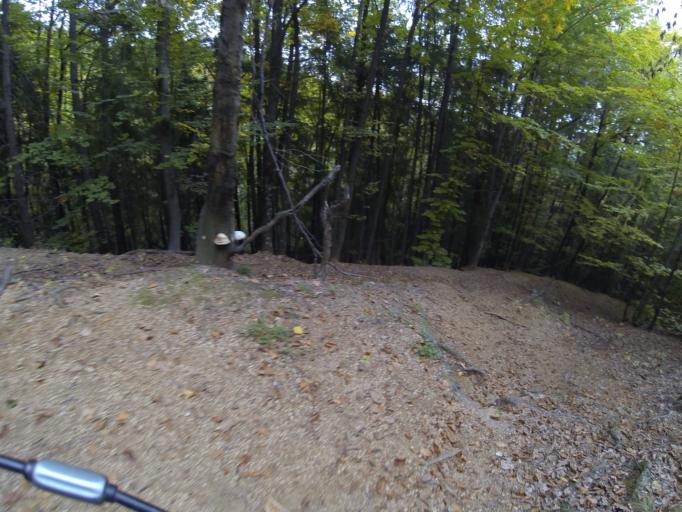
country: RO
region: Gorj
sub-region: Comuna Tismana
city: Sohodol
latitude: 45.0888
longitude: 22.8855
